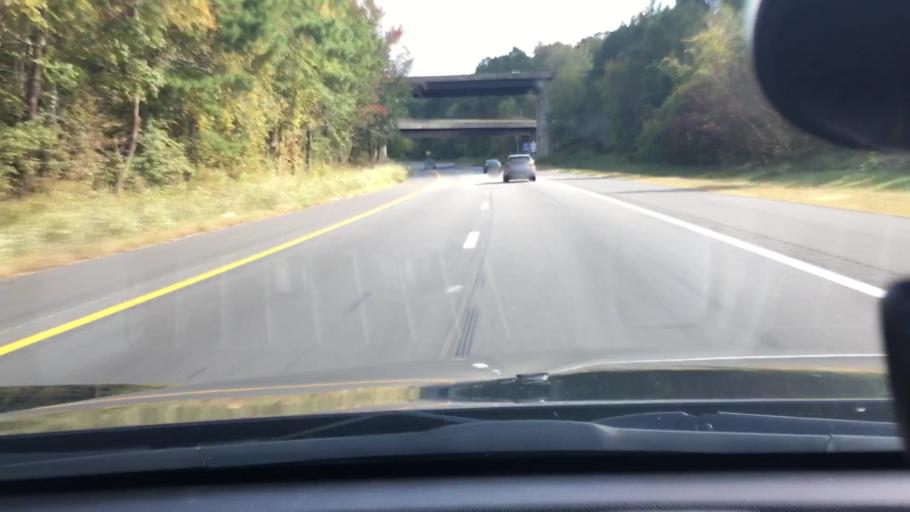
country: US
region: North Carolina
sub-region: Wake County
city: Raleigh
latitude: 35.7542
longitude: -78.5976
